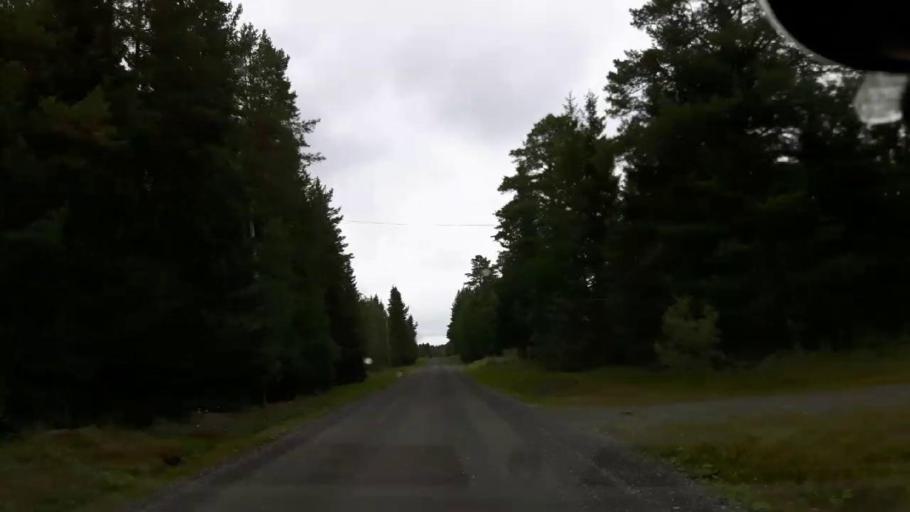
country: SE
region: Jaemtland
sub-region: OEstersunds Kommun
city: Ostersund
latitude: 63.0090
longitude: 14.5847
